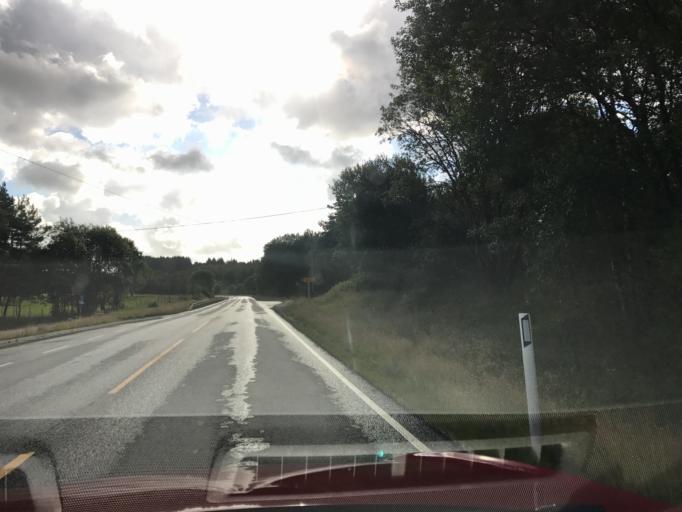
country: NO
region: Hordaland
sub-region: Sveio
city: Sveio
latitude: 59.5500
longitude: 5.3871
